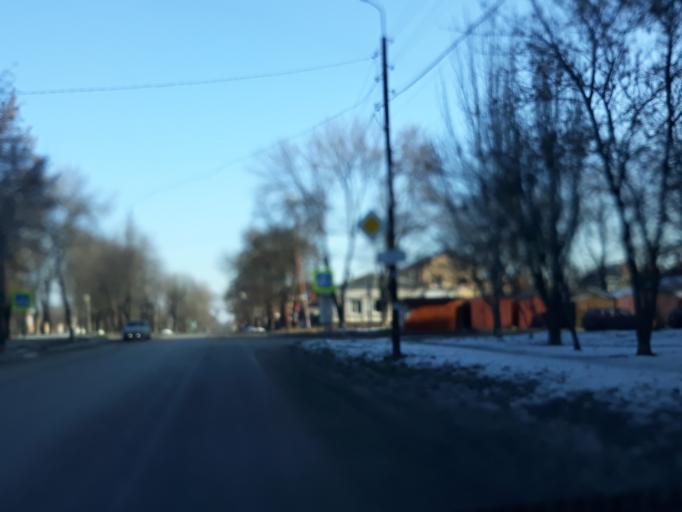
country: RU
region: Rostov
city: Taganrog
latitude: 47.2049
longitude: 38.9053
